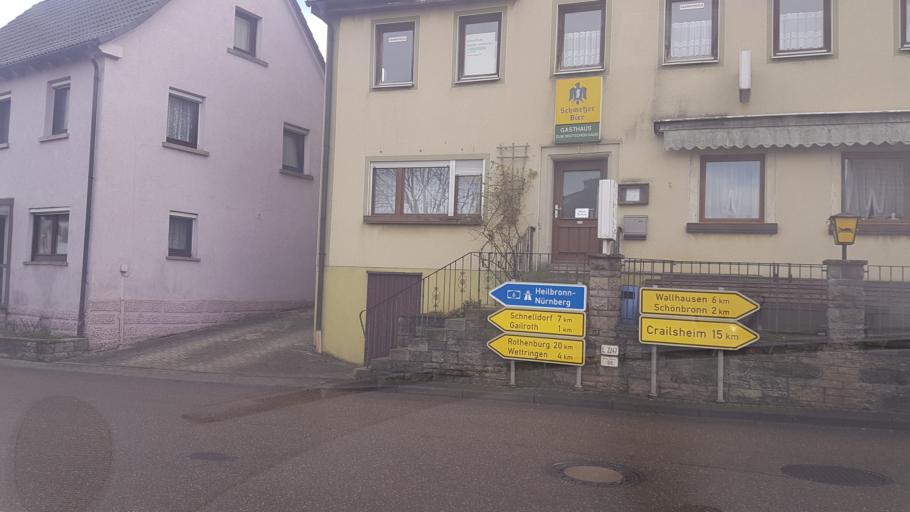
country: DE
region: Bavaria
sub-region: Regierungsbezirk Mittelfranken
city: Wettringen
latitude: 49.2346
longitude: 10.1196
